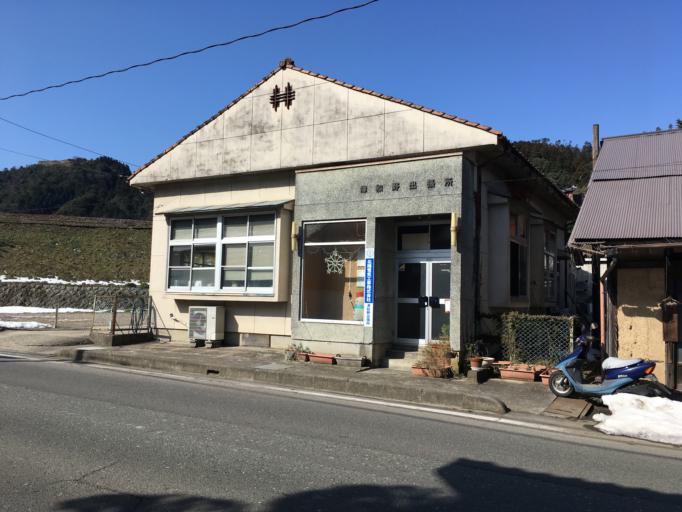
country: JP
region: Shimane
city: Masuda
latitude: 34.4647
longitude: 131.7731
